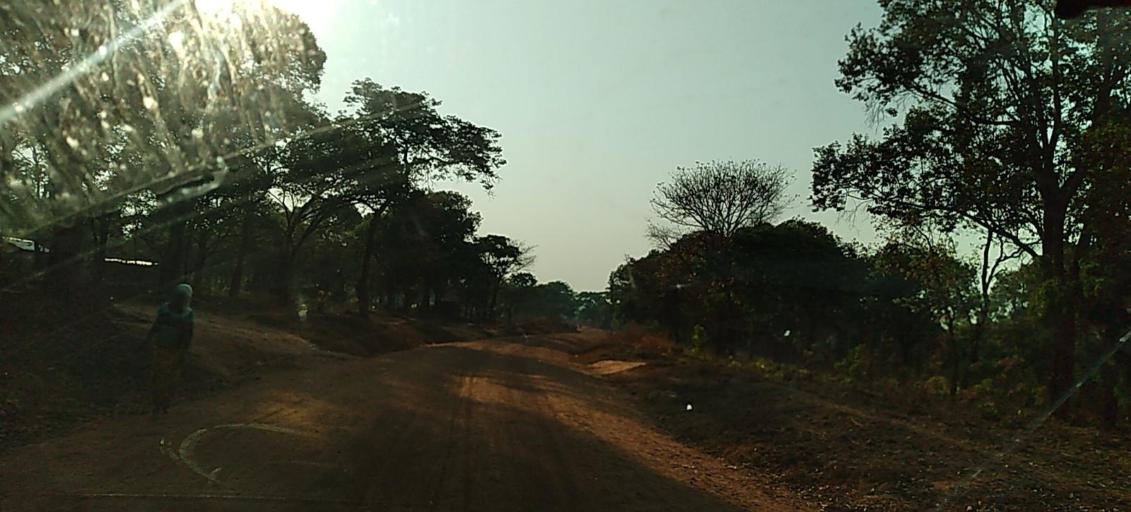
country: ZM
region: North-Western
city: Kasempa
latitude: -13.4722
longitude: 25.8722
